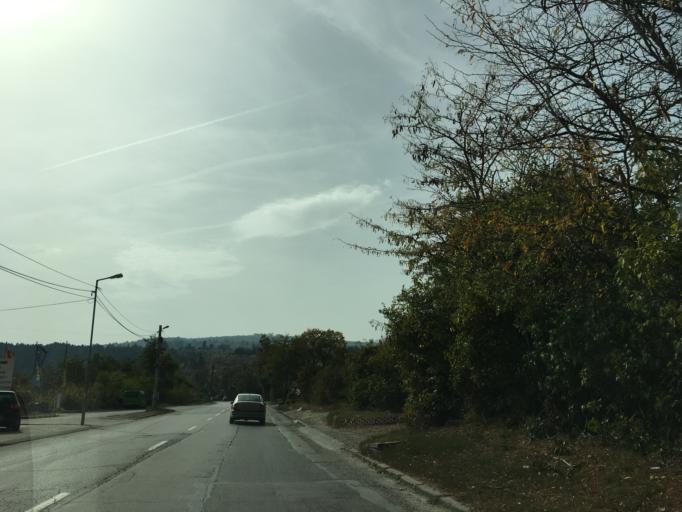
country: BG
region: Sofia-Capital
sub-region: Stolichna Obshtina
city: Sofia
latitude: 42.6144
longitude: 23.4005
